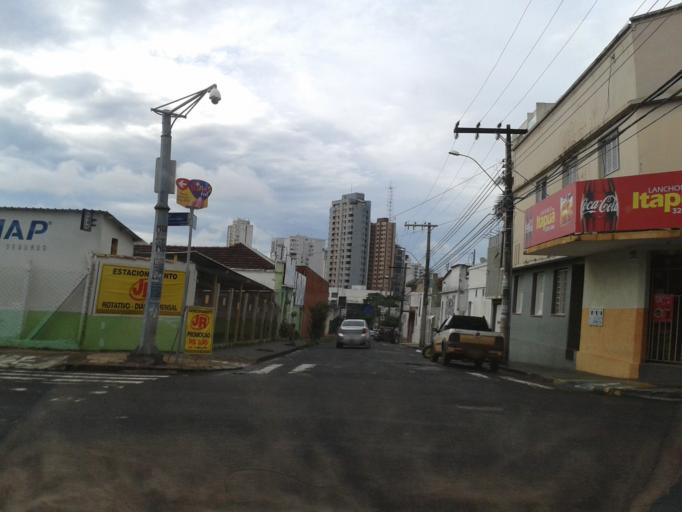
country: BR
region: Minas Gerais
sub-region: Uberlandia
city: Uberlandia
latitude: -18.9130
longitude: -48.2801
